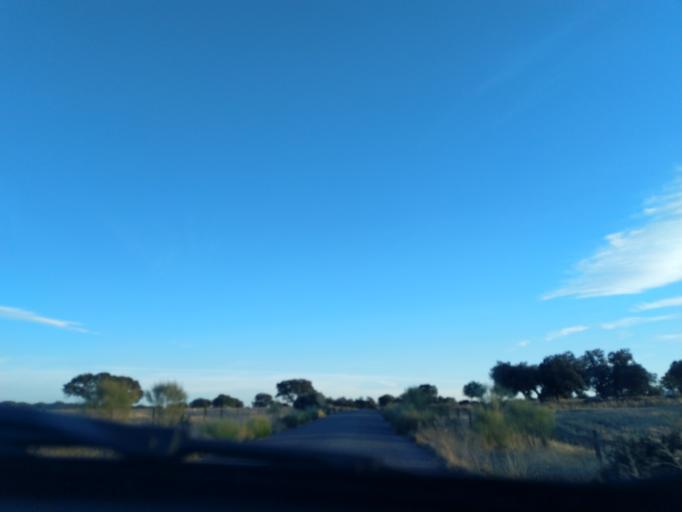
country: ES
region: Extremadura
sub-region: Provincia de Badajoz
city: Valverde de Llerena
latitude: 38.2442
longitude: -5.8249
